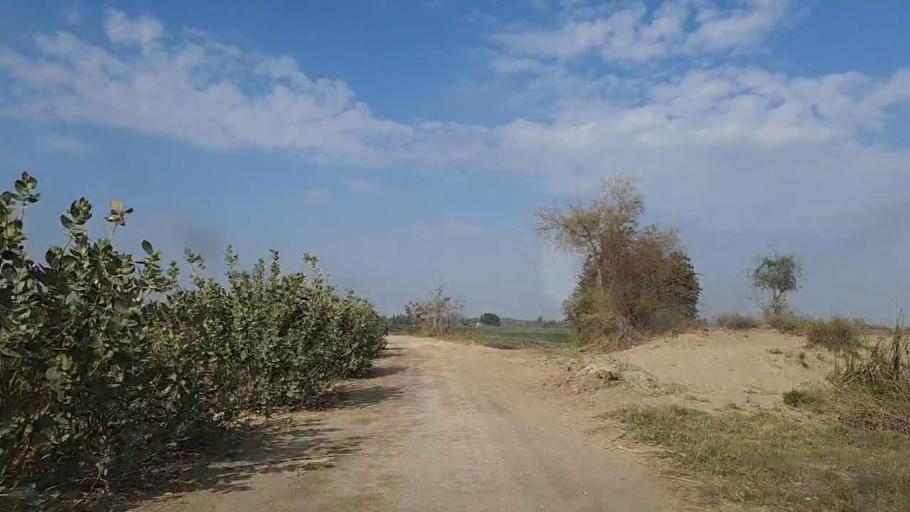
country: PK
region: Sindh
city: Sanghar
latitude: 26.2717
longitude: 69.0121
